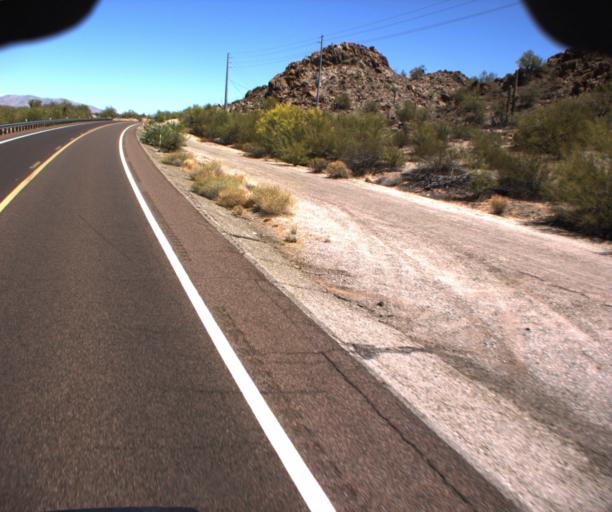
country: US
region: Arizona
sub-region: La Paz County
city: Salome
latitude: 33.7492
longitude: -113.6720
